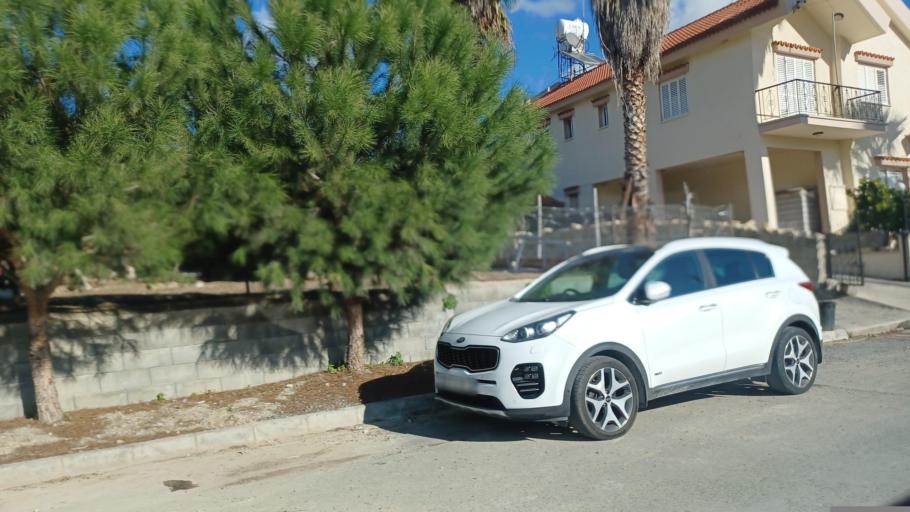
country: CY
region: Limassol
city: Pano Polemidia
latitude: 34.7631
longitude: 32.9976
